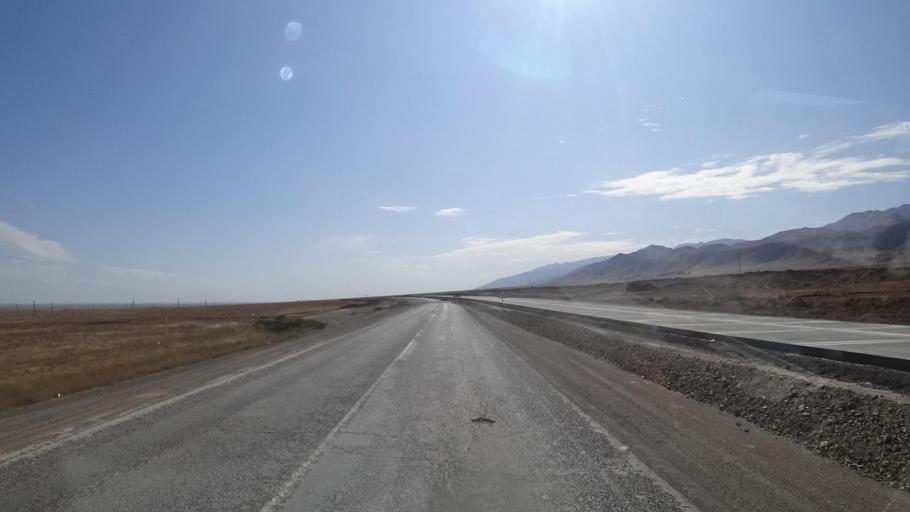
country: KG
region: Chuy
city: Ivanovka
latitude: 43.3879
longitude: 75.1489
